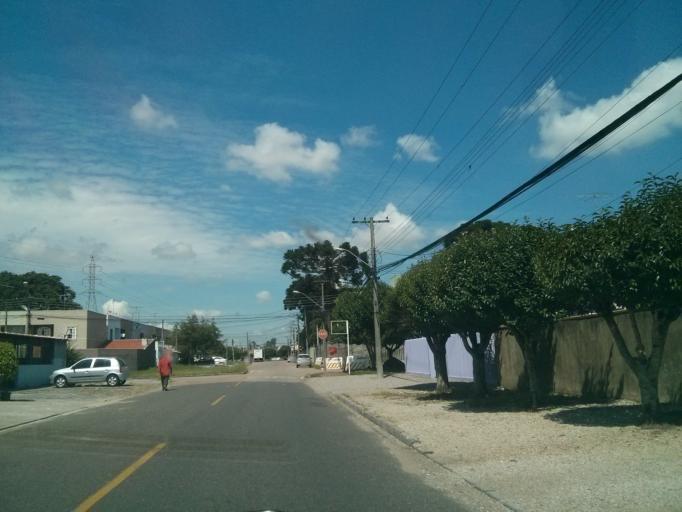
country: BR
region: Parana
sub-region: Sao Jose Dos Pinhais
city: Sao Jose dos Pinhais
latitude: -25.5244
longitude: -49.2298
